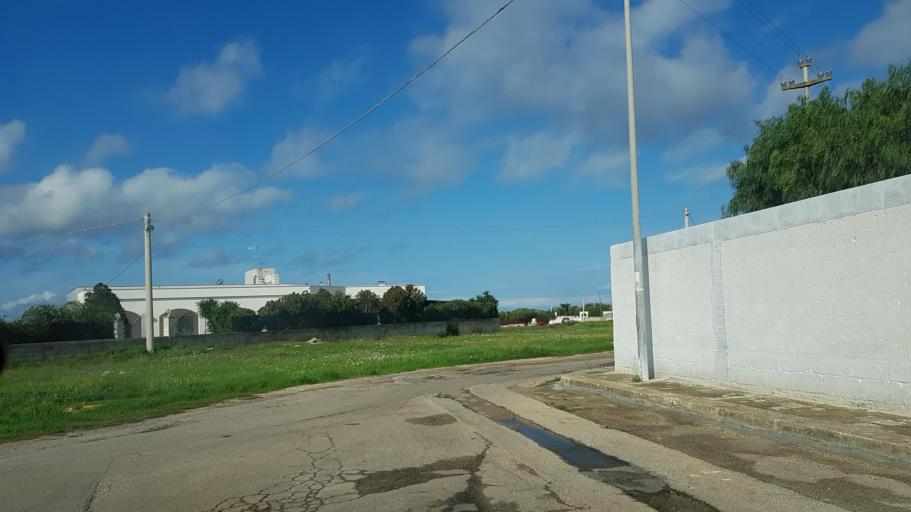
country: IT
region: Apulia
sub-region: Provincia di Brindisi
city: Carovigno
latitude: 40.7154
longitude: 17.6556
